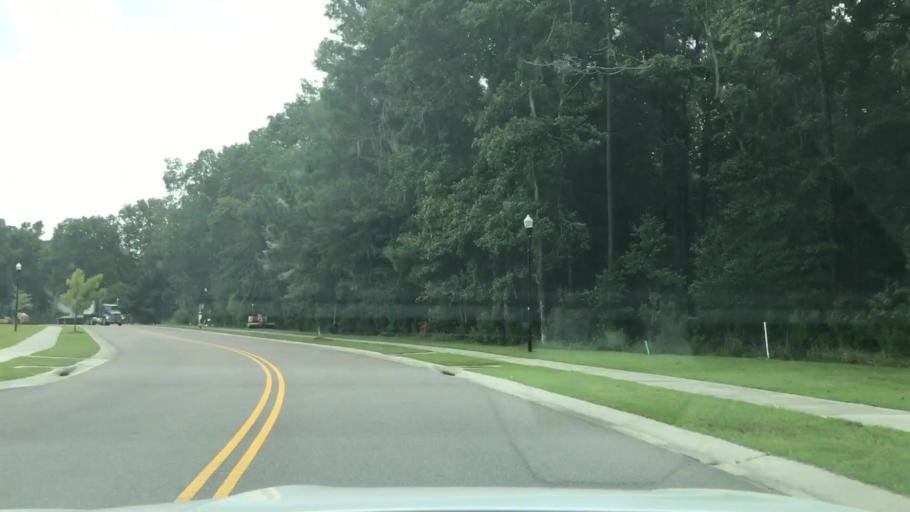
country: US
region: South Carolina
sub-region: Charleston County
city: Shell Point
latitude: 32.8283
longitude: -80.0982
